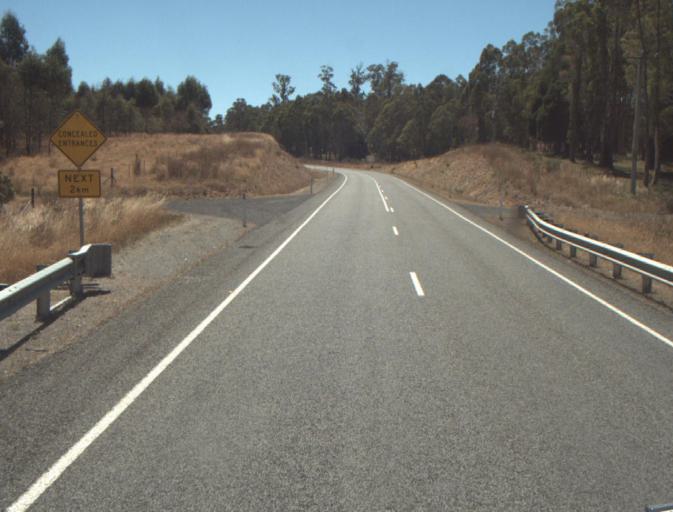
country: AU
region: Tasmania
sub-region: Launceston
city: Newstead
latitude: -41.3413
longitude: 147.3461
